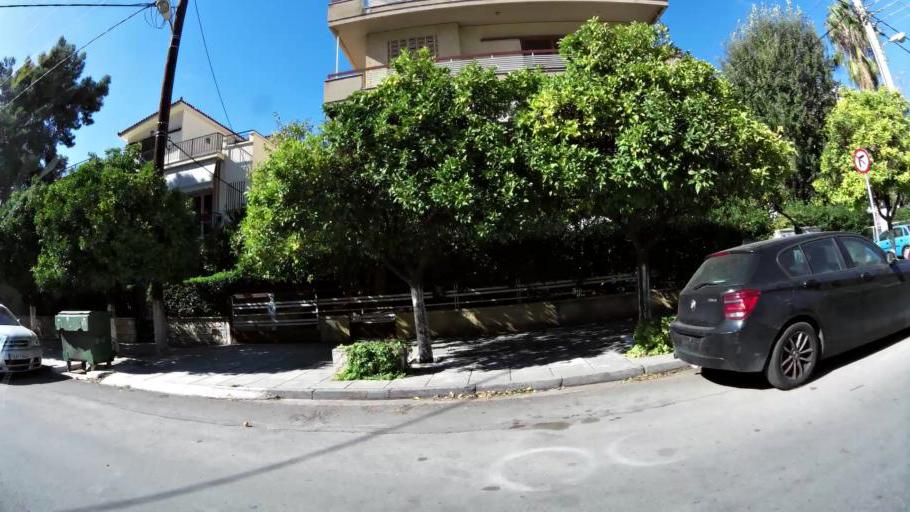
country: GR
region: Attica
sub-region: Nomarchia Athinas
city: Vrilissia
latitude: 38.0272
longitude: 23.8190
